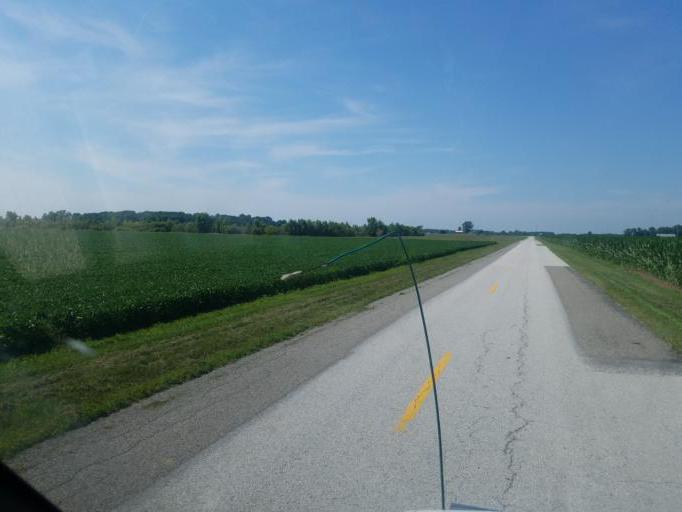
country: US
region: Ohio
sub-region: Logan County
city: Lakeview
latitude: 40.5514
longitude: -84.0120
